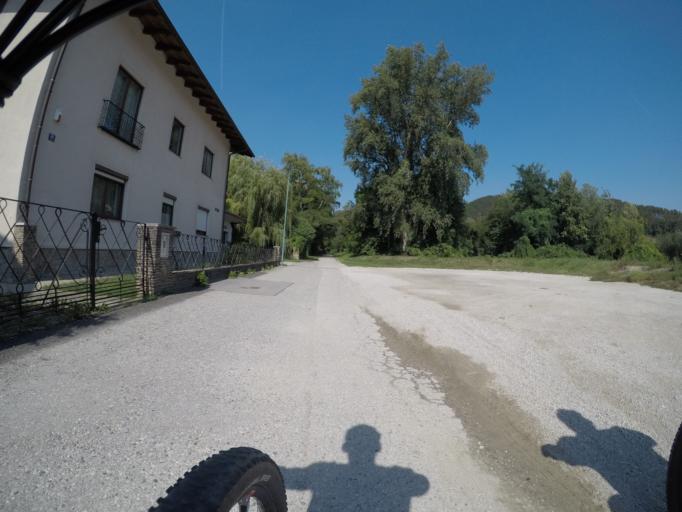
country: AT
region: Lower Austria
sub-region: Politischer Bezirk Baden
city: Berndorf
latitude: 47.9373
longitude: 16.1419
